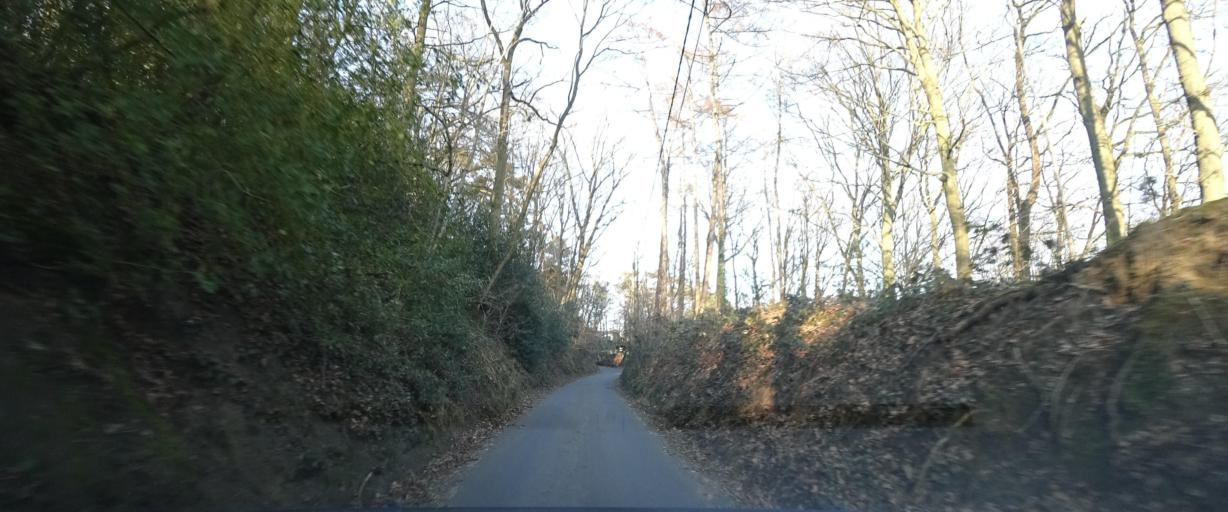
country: BE
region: Wallonia
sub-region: Province du Brabant Wallon
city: Louvain-la-Neuve
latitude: 50.6540
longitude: 4.5962
